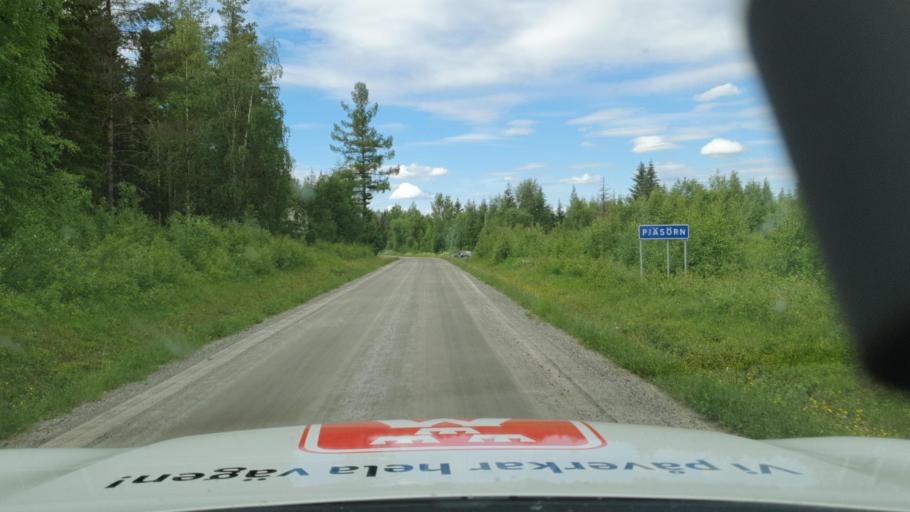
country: SE
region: Vaesterbotten
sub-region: Norsjo Kommun
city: Norsjoe
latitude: 64.8400
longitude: 19.7021
